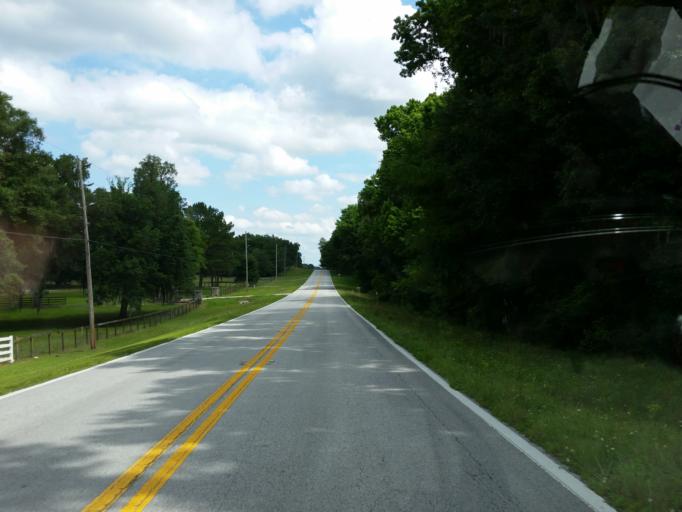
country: US
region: Florida
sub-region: Citrus County
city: Floral City
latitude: 28.6762
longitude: -82.3600
